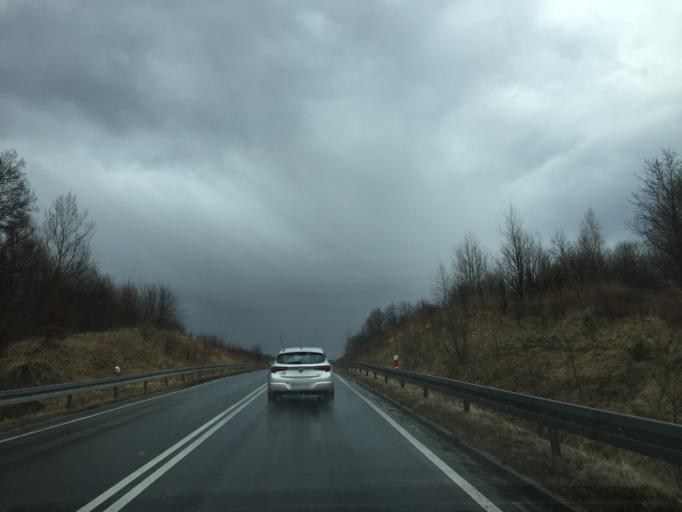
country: PL
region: Lesser Poland Voivodeship
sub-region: Powiat suski
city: Zembrzyce
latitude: 49.7702
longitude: 19.6046
